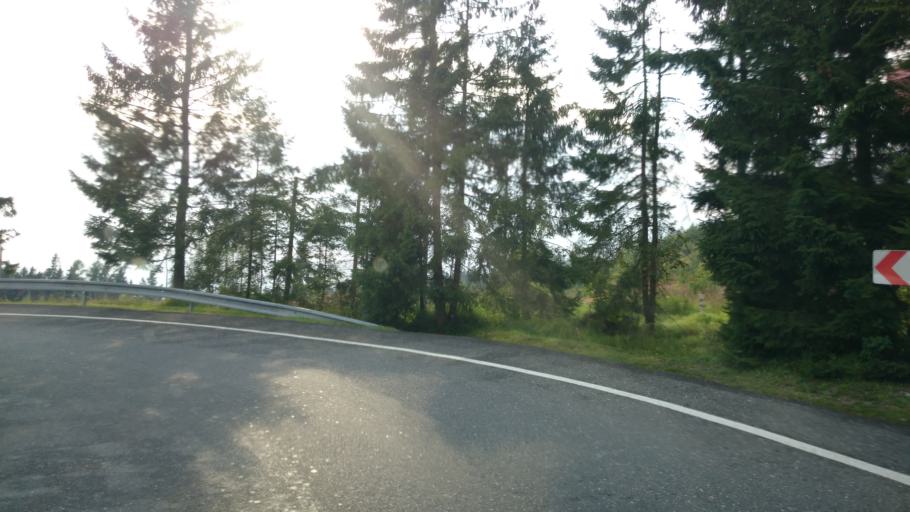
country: SK
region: Presovsky
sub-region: Okres Poprad
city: Strba
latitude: 49.1141
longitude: 20.0673
